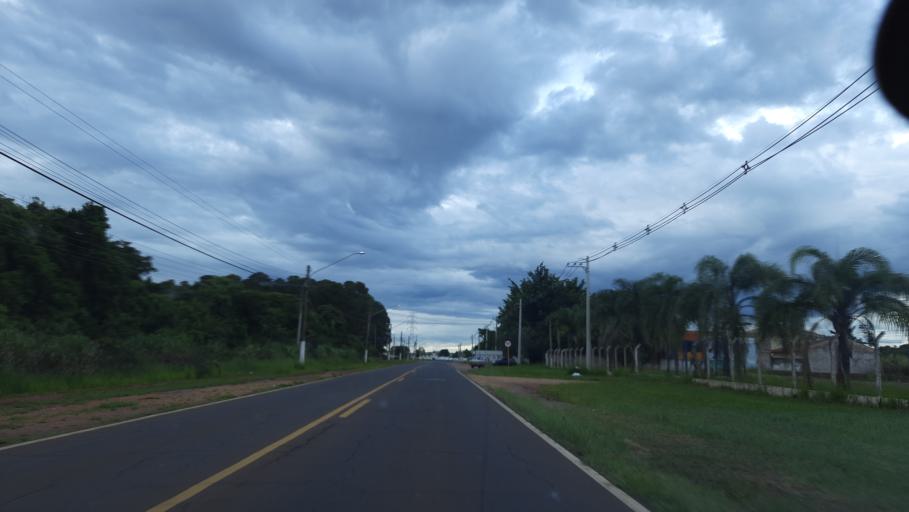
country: BR
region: Sao Paulo
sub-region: Casa Branca
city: Casa Branca
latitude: -21.7734
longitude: -47.0696
